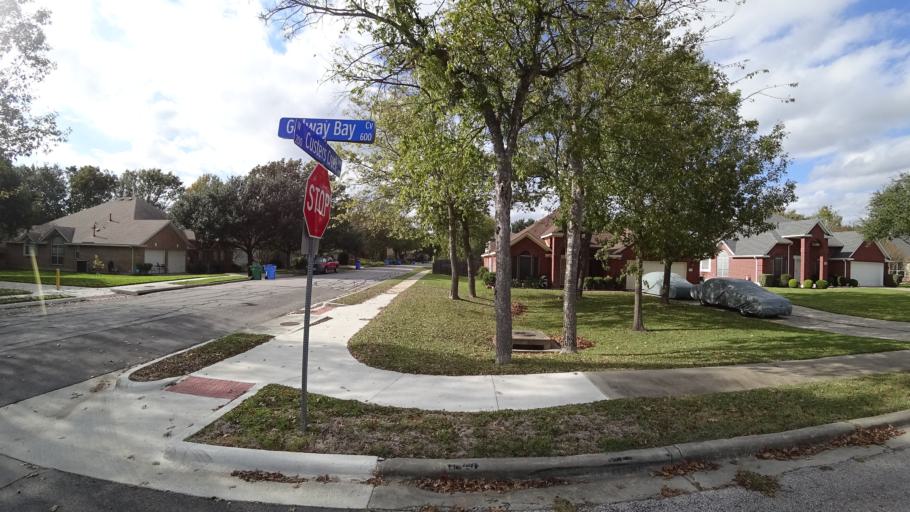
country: US
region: Texas
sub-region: Travis County
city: Pflugerville
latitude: 30.4357
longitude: -97.6256
